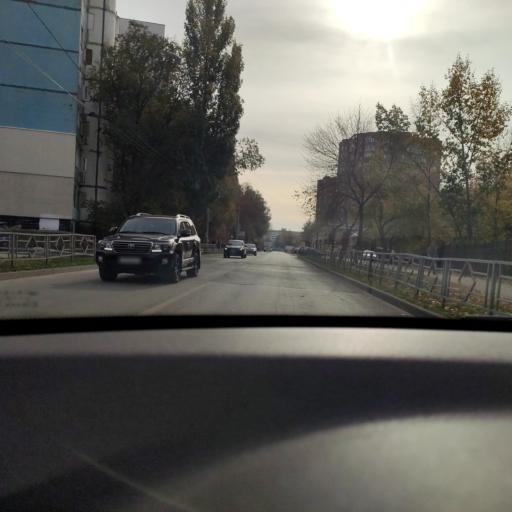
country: RU
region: Samara
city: Samara
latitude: 53.2491
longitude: 50.2098
